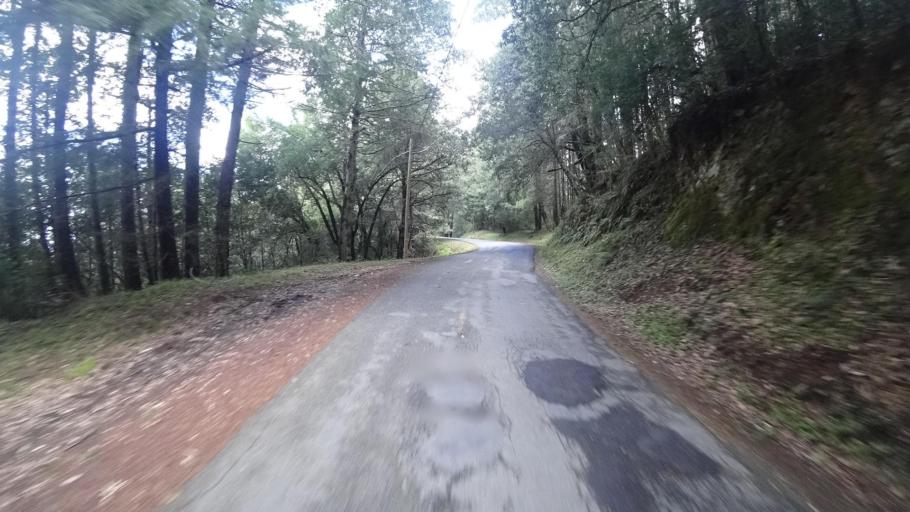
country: US
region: California
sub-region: Humboldt County
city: Bayside
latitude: 40.7548
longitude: -123.9712
